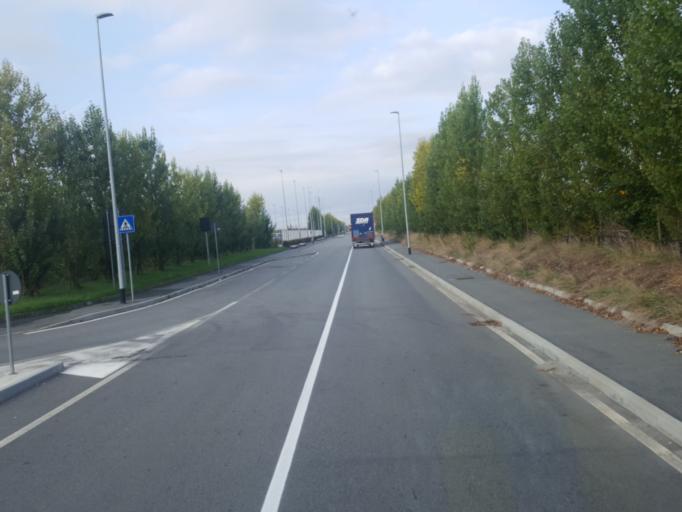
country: IT
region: Piedmont
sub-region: Provincia di Vercelli
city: Asigliano Vercellese
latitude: 45.2928
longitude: 8.3989
